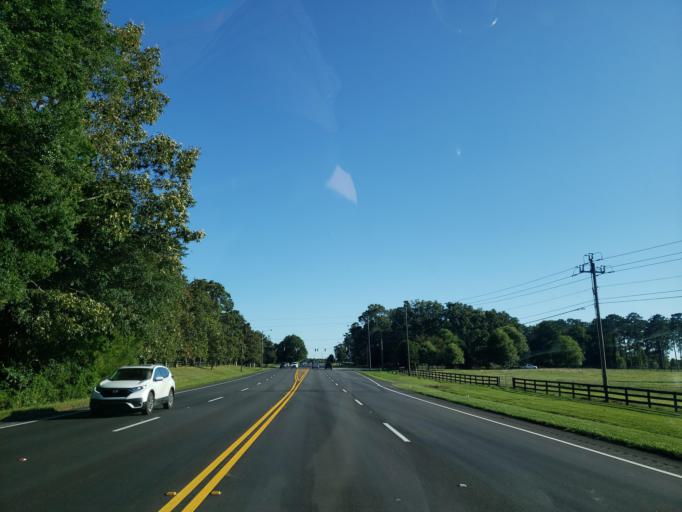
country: US
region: Georgia
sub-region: Floyd County
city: Rome
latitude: 34.2915
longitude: -85.1798
